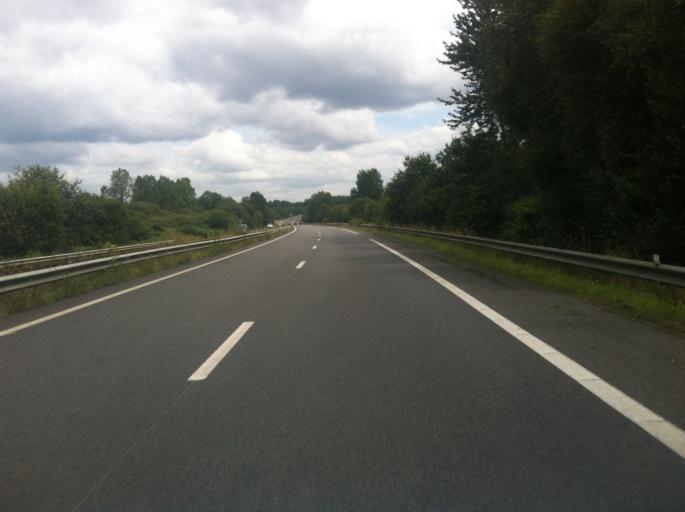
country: FR
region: Brittany
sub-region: Departement des Cotes-d'Armor
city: Plounevez-Moedec
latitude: 48.5622
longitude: -3.5173
